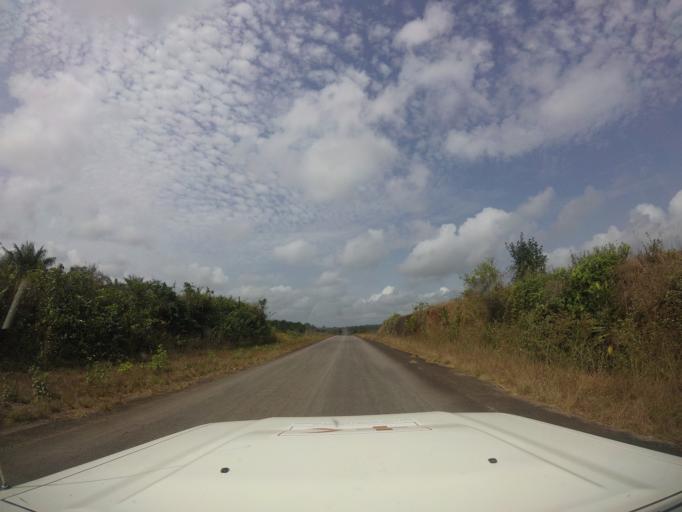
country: LR
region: Bomi
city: Tubmanburg
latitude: 6.7252
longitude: -11.0476
